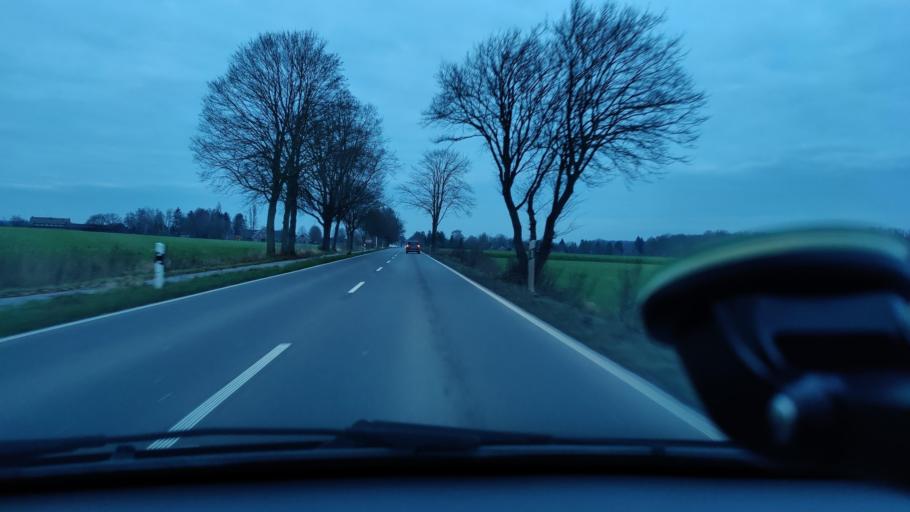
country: DE
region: North Rhine-Westphalia
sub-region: Regierungsbezirk Dusseldorf
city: Grefrath
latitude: 51.3068
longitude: 6.3558
